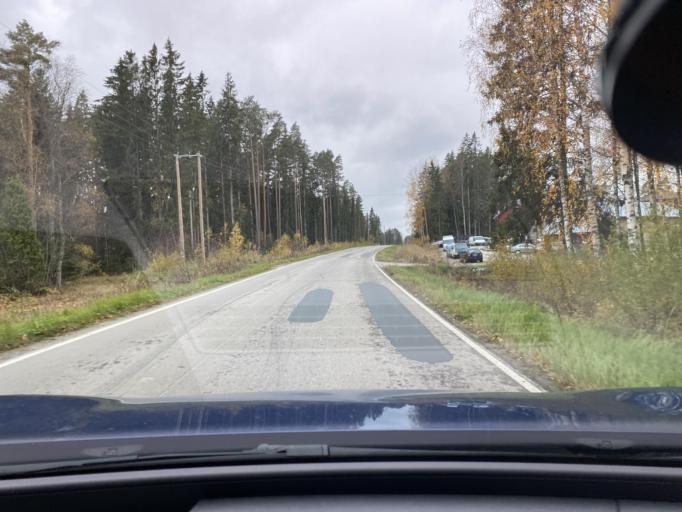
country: FI
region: Varsinais-Suomi
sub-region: Vakka-Suomi
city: Pyhaeranta
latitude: 60.9174
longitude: 21.5708
